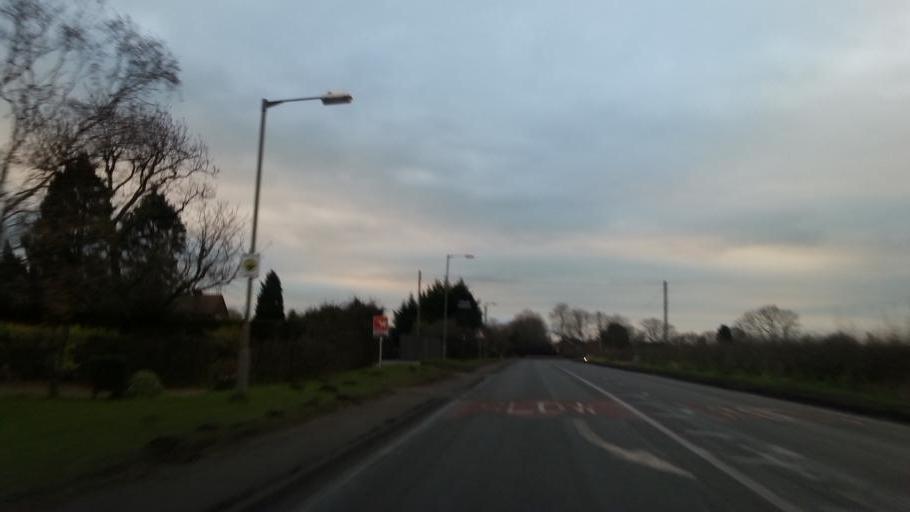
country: GB
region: England
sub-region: Nottinghamshire
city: Newark on Trent
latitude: 53.1100
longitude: -0.8202
